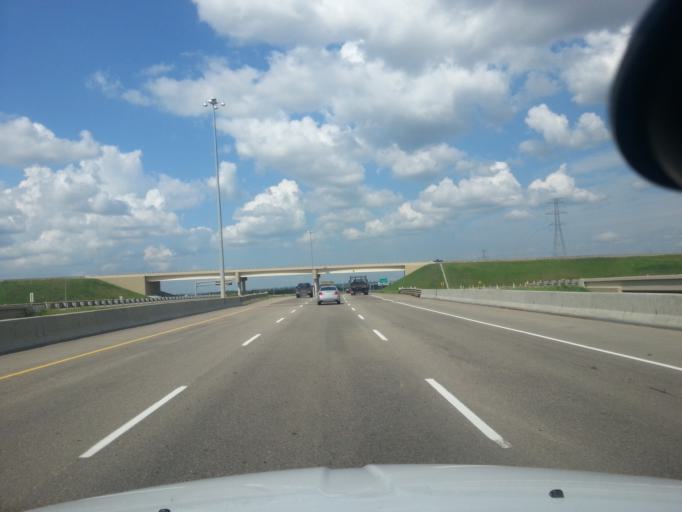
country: CA
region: Alberta
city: St. Albert
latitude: 53.5737
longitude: -113.6614
